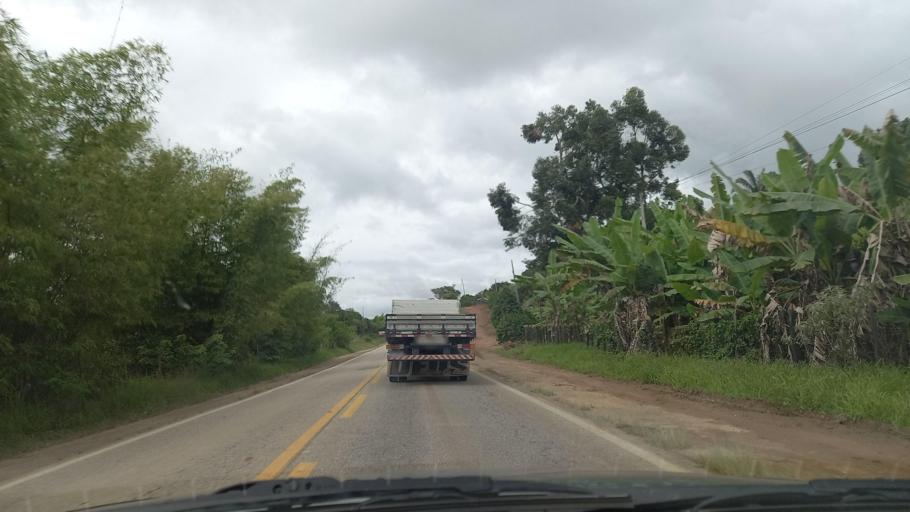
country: BR
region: Pernambuco
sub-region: Canhotinho
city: Canhotinho
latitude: -8.8568
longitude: -36.1744
